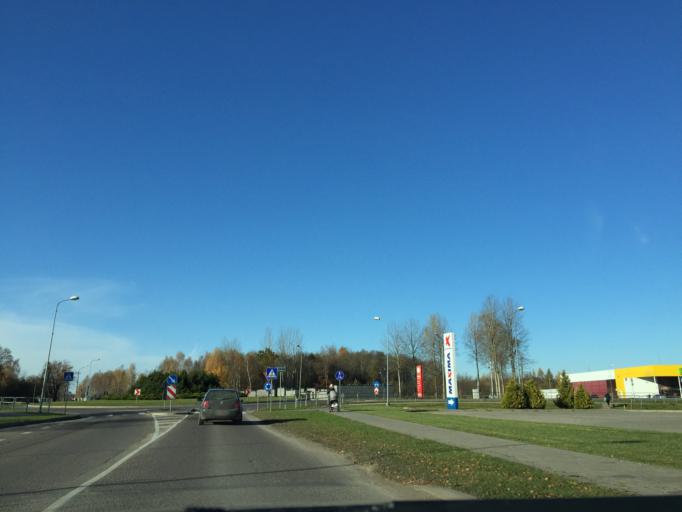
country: LV
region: Aizkraukles Rajons
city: Aizkraukle
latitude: 56.6081
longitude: 25.2589
